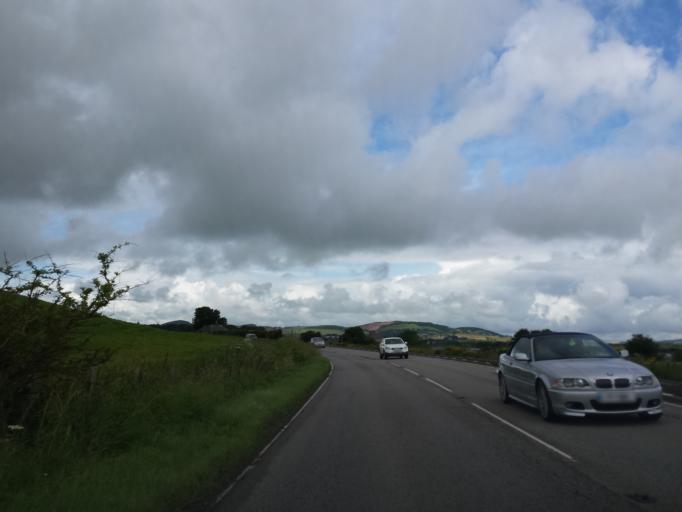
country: GB
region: Scotland
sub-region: Fife
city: Strathkinness
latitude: 56.3585
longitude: -2.8667
